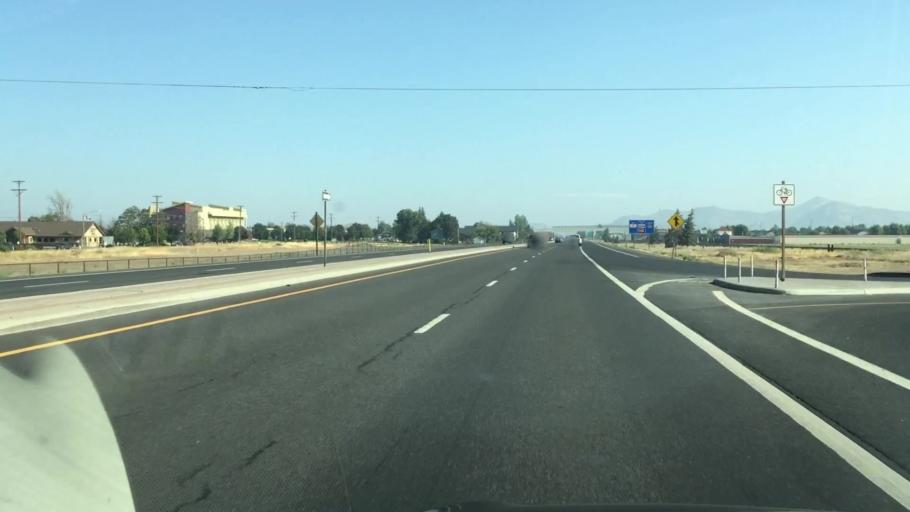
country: US
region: Oregon
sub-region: Deschutes County
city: Redmond
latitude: 44.2836
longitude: -121.1680
